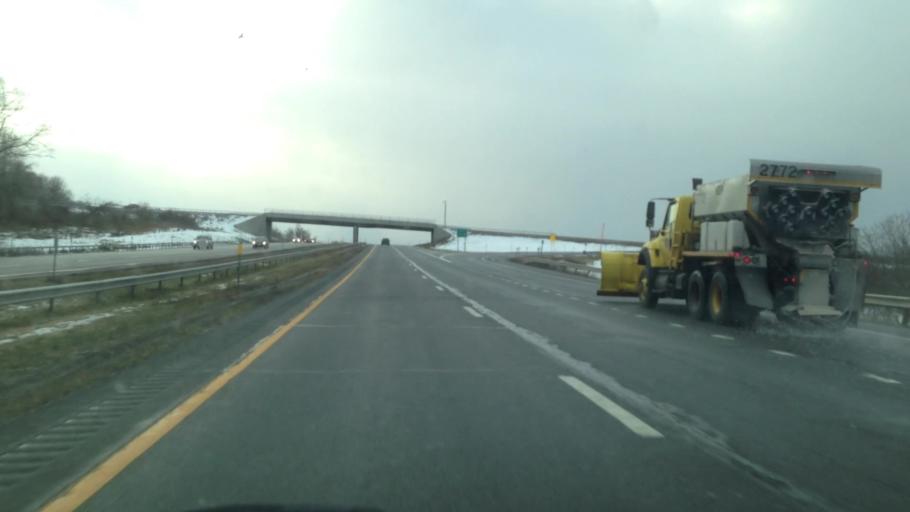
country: US
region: New York
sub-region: Montgomery County
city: Amsterdam
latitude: 42.9222
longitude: -74.1928
